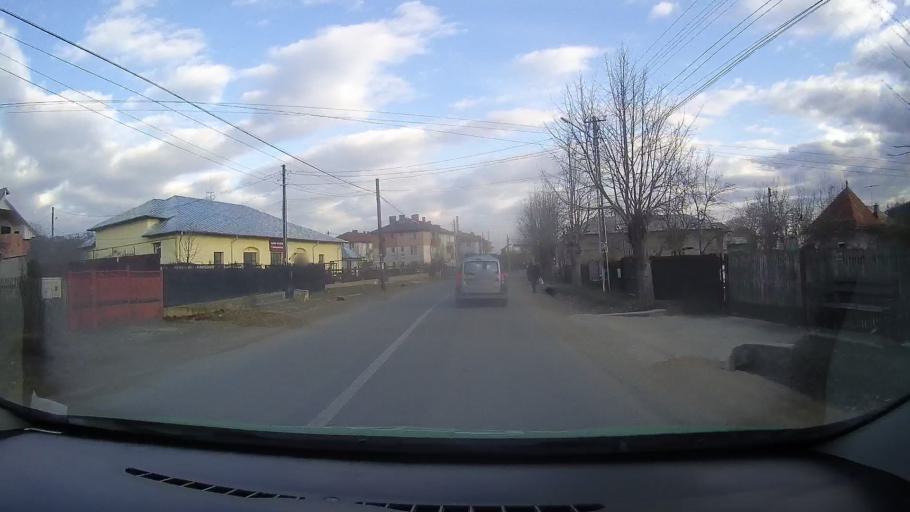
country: RO
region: Dambovita
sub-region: Comuna Gura Ocnitei
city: Gura Ocnitei
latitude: 44.9456
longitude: 25.5604
